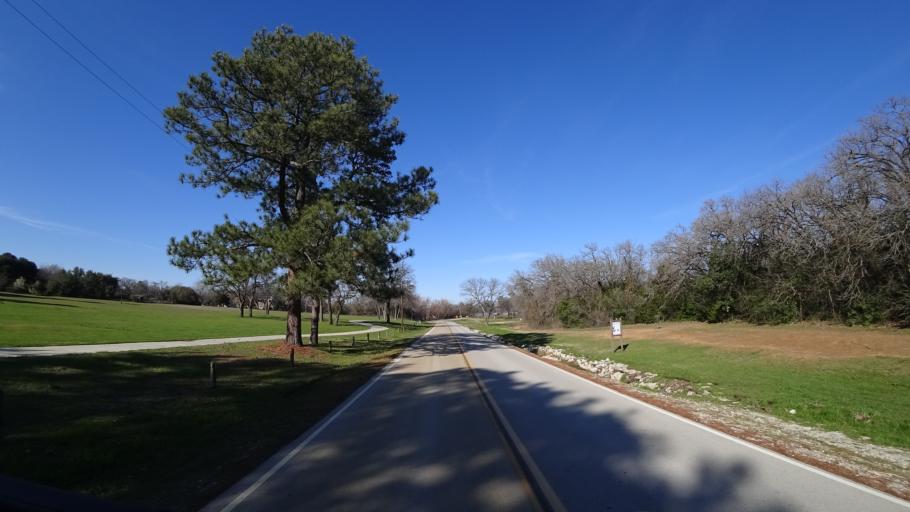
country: US
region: Texas
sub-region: Denton County
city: Lewisville
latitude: 33.0769
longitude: -97.0111
